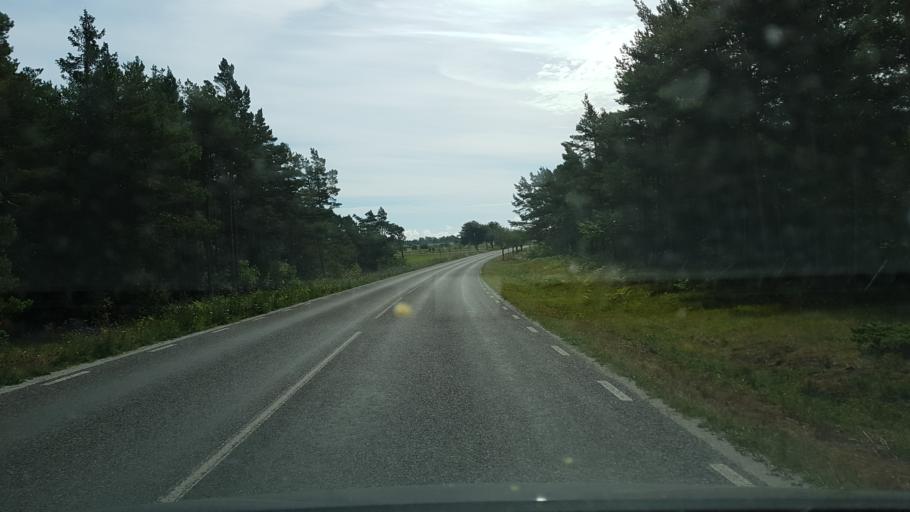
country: SE
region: Gotland
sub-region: Gotland
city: Hemse
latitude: 57.4328
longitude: 18.6145
